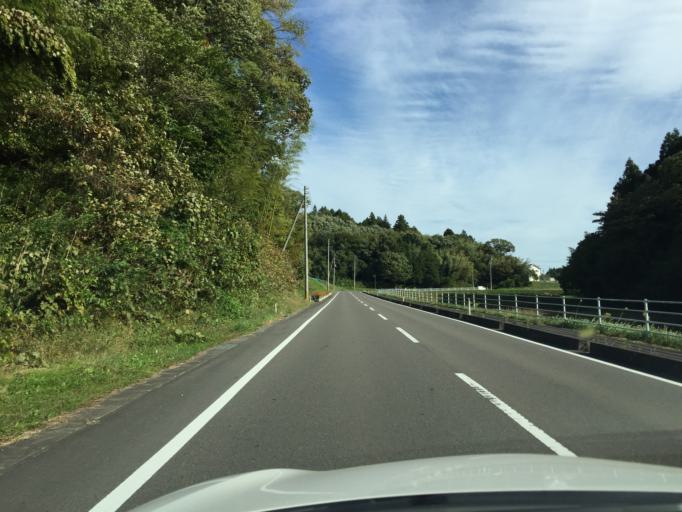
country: JP
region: Fukushima
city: Miharu
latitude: 37.4284
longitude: 140.4625
